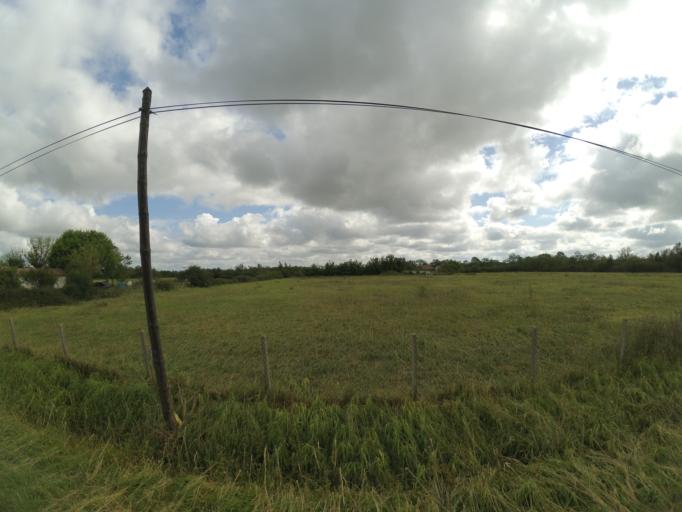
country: FR
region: Aquitaine
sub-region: Departement de la Gironde
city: Ludon-Medoc
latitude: 44.9987
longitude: -0.5953
